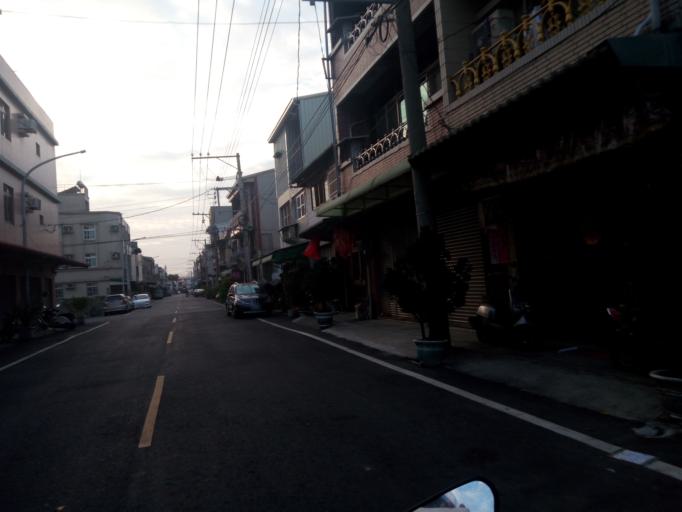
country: TW
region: Taiwan
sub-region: Chiayi
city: Jiayi Shi
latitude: 23.4989
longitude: 120.3874
